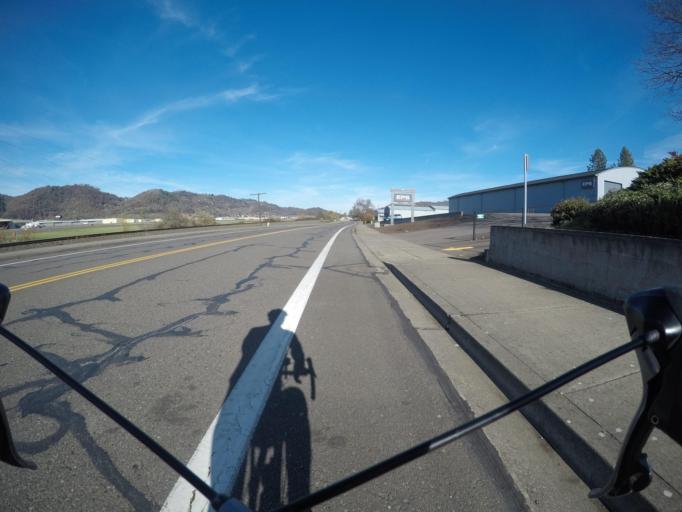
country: US
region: Oregon
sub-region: Douglas County
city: Roseburg
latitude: 43.2349
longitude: -123.3545
